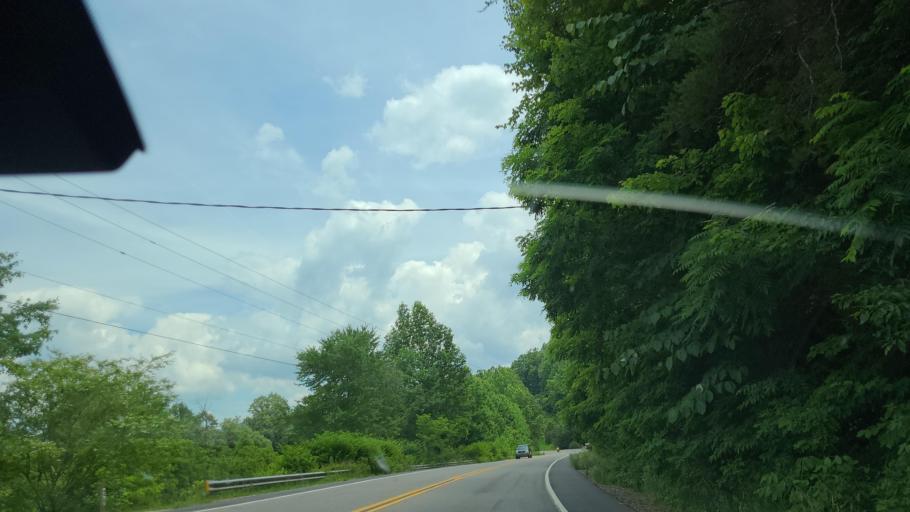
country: US
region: North Carolina
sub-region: Macon County
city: Franklin
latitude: 35.1548
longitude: -83.3152
